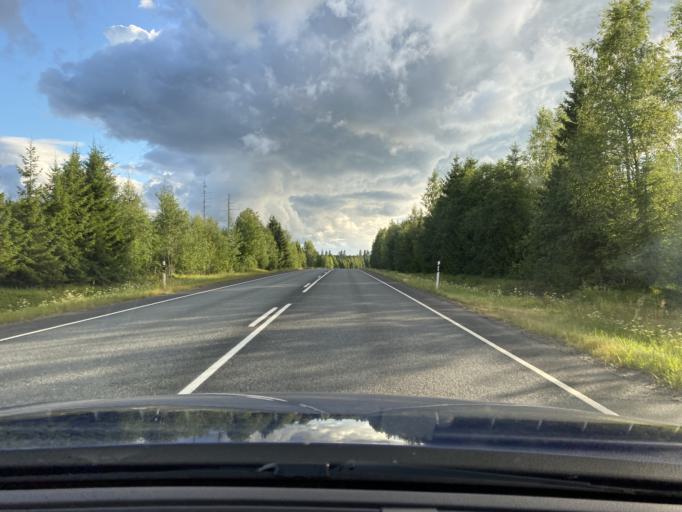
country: FI
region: Haeme
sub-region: Haemeenlinna
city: Renko
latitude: 60.8534
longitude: 24.1600
